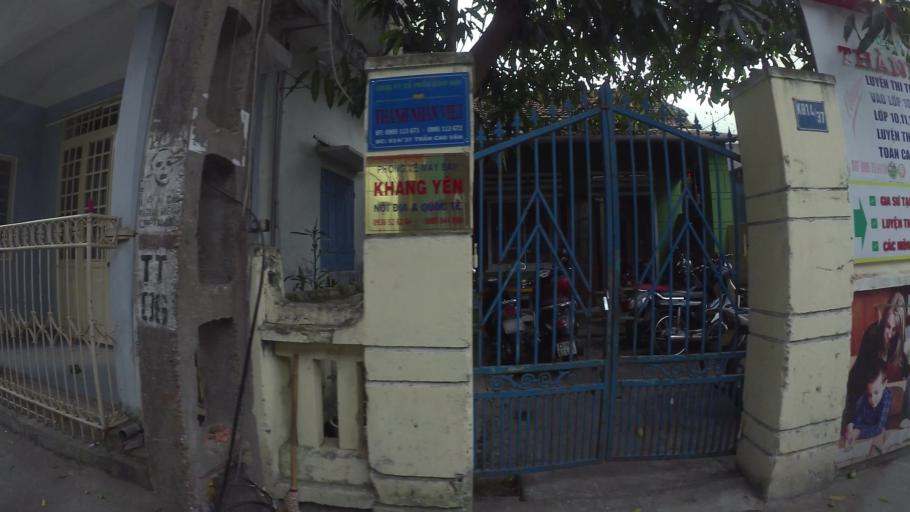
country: VN
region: Da Nang
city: Thanh Khe
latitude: 16.0709
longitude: 108.1837
